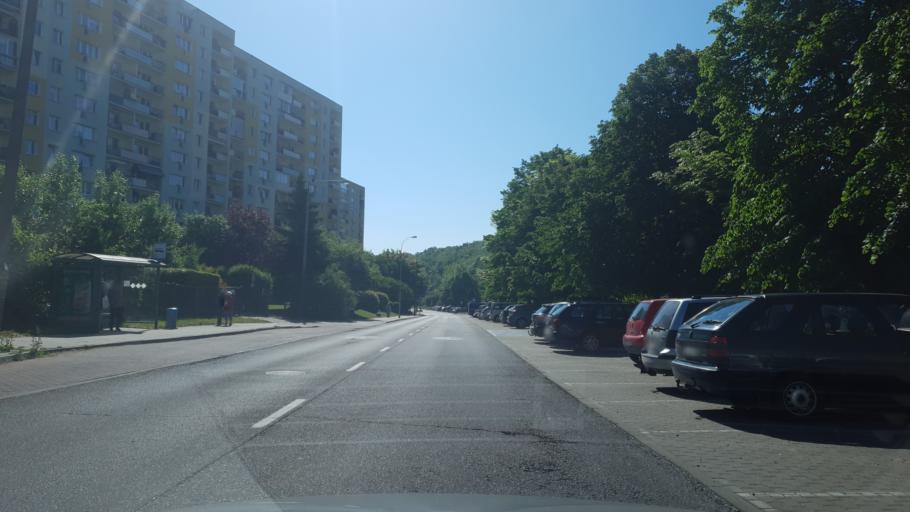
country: PL
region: Pomeranian Voivodeship
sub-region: Sopot
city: Sopot
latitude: 54.4572
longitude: 18.5375
